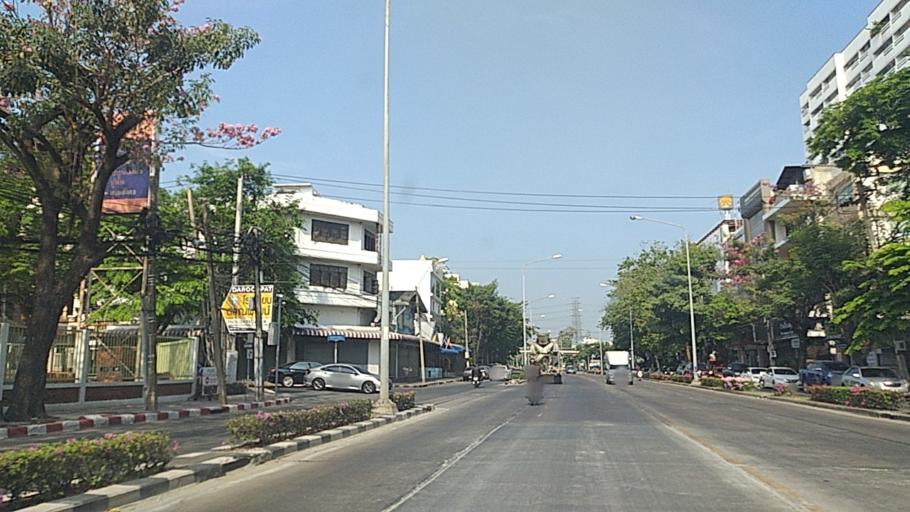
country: TH
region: Bangkok
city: Chatuchak
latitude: 13.8400
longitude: 100.5483
